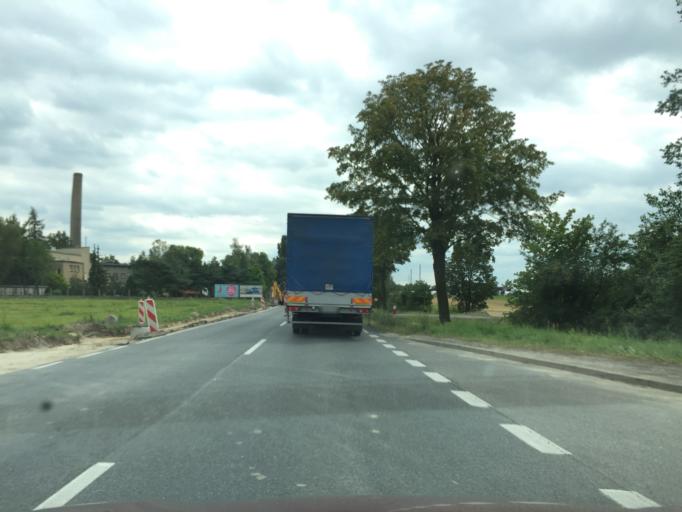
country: PL
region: Greater Poland Voivodeship
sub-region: Kalisz
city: Kalisz
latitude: 51.7946
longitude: 18.0913
